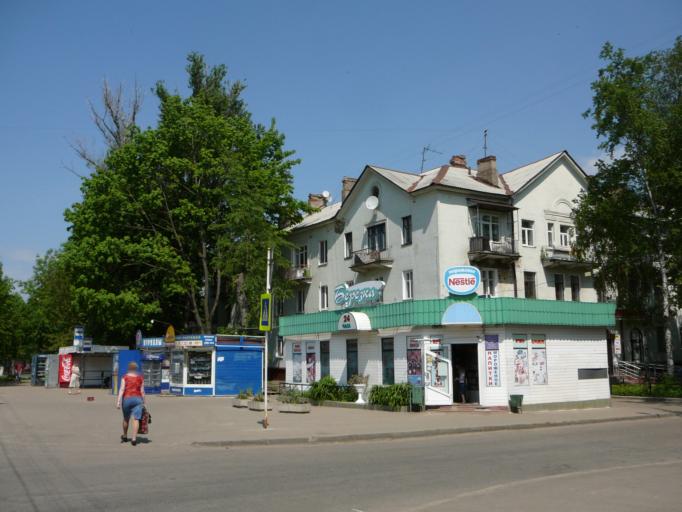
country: RU
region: Smolensk
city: Smolensk
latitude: 54.7768
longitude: 32.0238
